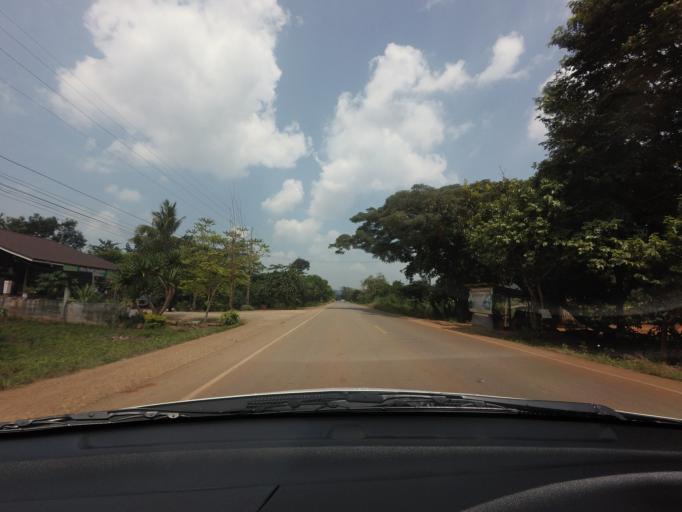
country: TH
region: Nakhon Ratchasima
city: Pak Chong
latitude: 14.5678
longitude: 101.5703
